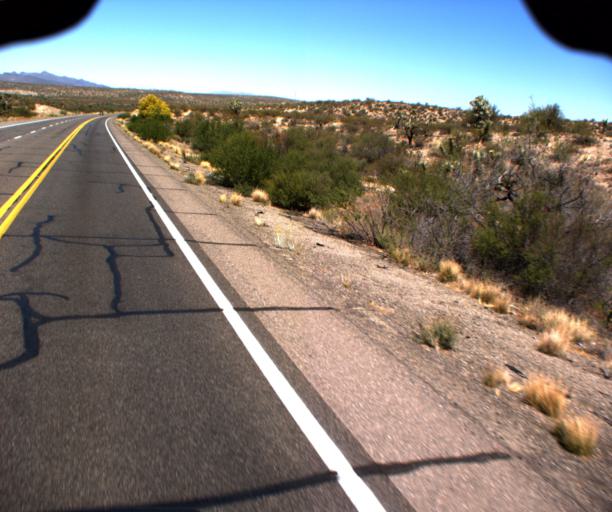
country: US
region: Arizona
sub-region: Yavapai County
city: Congress
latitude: 34.1933
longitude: -113.0556
